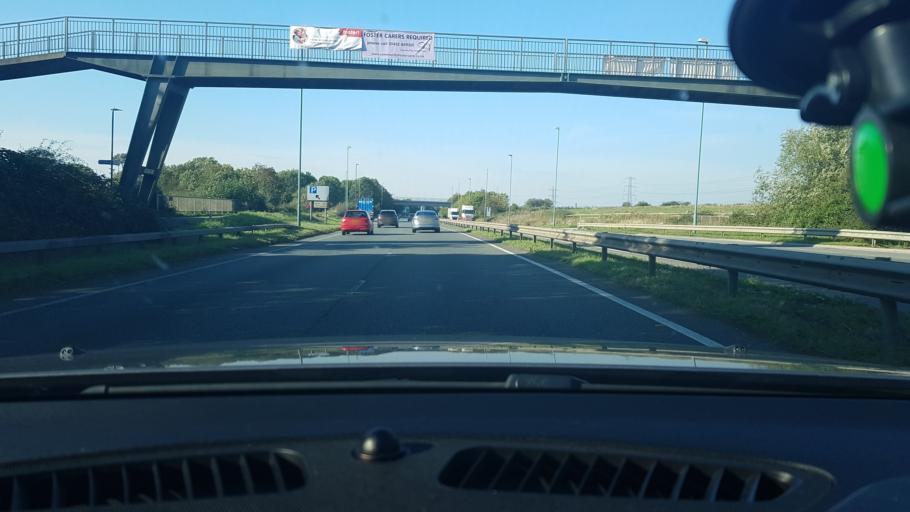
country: GB
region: England
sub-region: Gloucestershire
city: Barnwood
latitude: 51.8689
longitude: -2.1968
